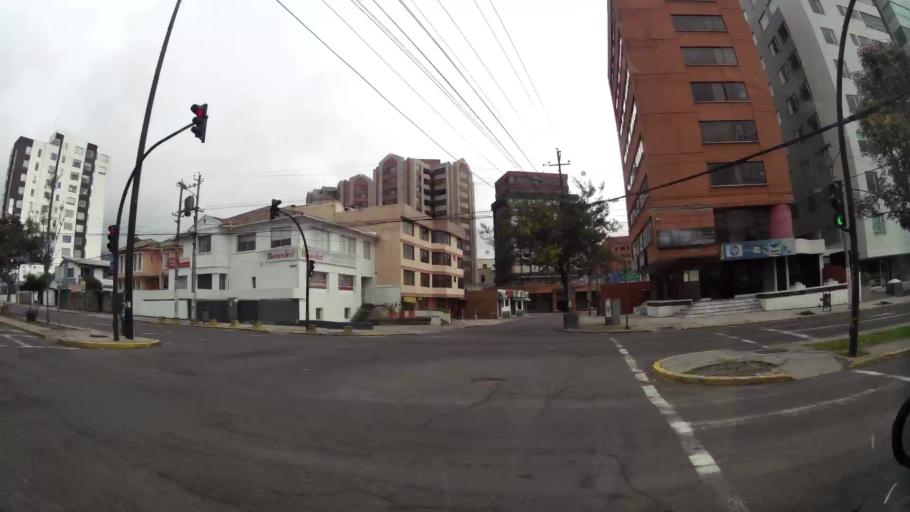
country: EC
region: Pichincha
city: Quito
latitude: -0.1965
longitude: -78.4930
